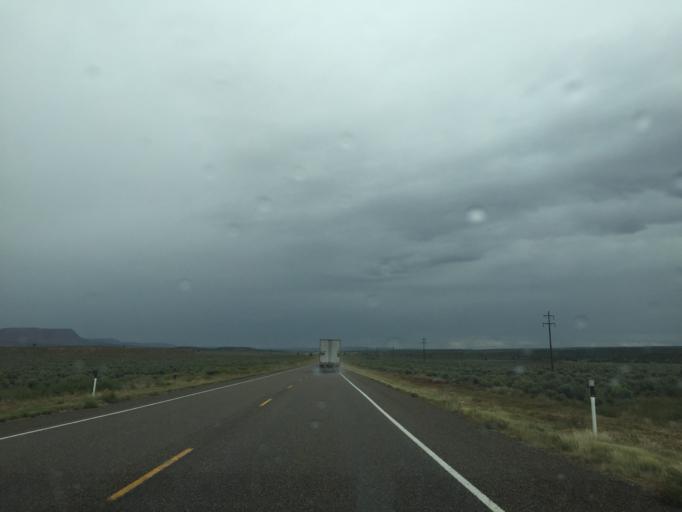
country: US
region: Utah
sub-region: Kane County
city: Kanab
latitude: 37.1147
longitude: -112.1119
